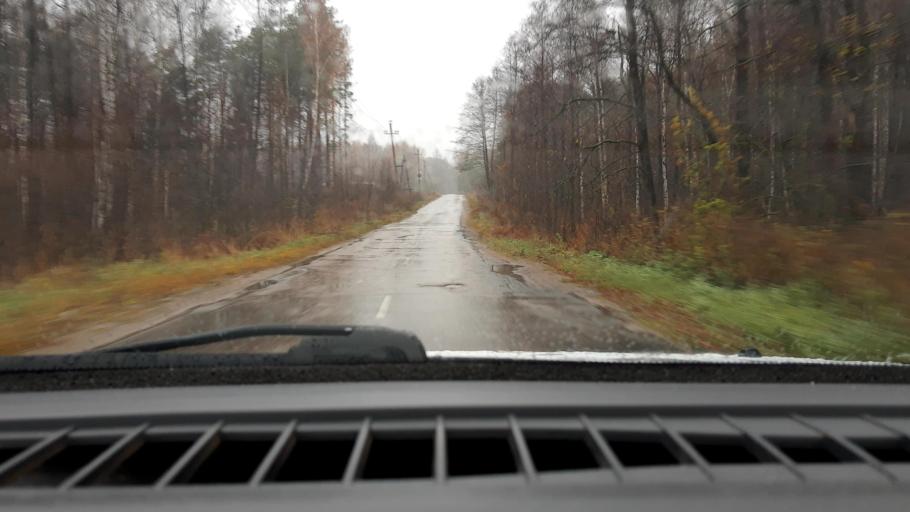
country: RU
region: Nizjnij Novgorod
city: Linda
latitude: 56.6873
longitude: 44.2026
